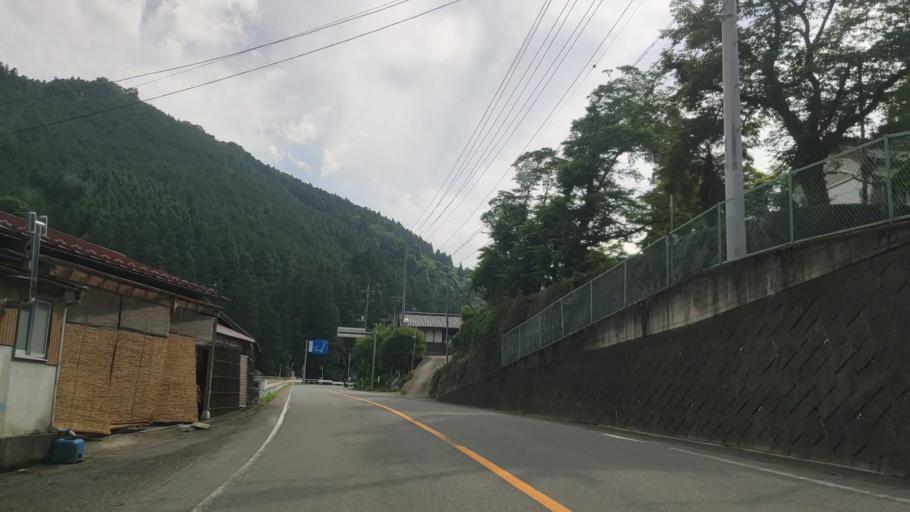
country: JP
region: Gunma
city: Tomioka
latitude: 36.1667
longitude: 138.7280
